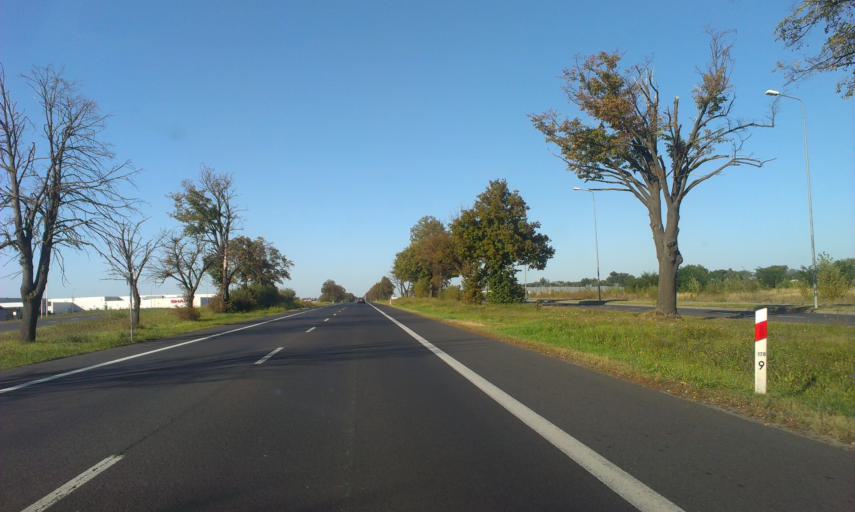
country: PL
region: Kujawsko-Pomorskie
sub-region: Powiat torunski
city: Lysomice
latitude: 53.1014
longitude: 18.6228
